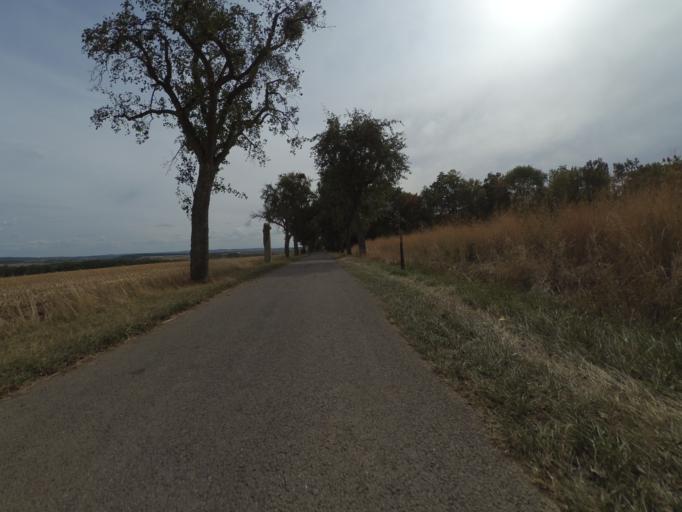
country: LU
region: Grevenmacher
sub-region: Canton de Remich
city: Mondorf-les-Bains
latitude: 49.4977
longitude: 6.2946
